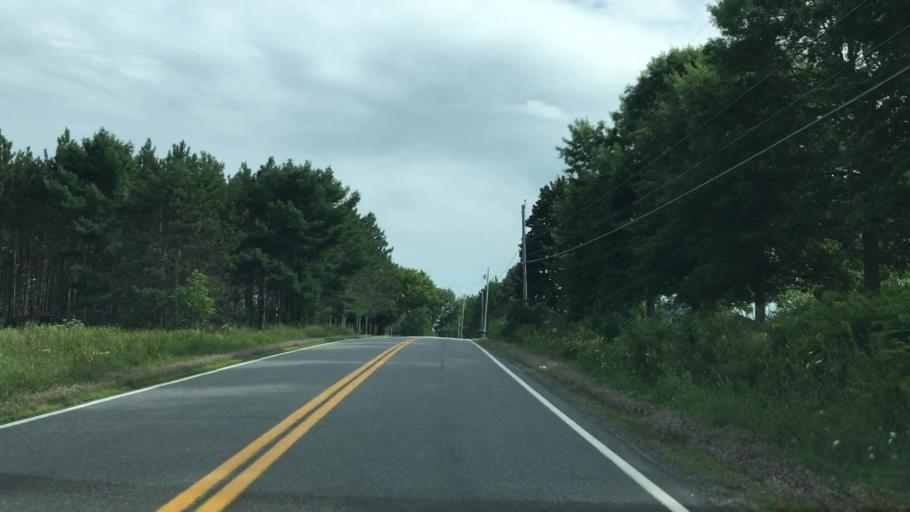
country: US
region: Maine
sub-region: Waldo County
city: Belfast
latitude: 44.3799
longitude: -69.0344
